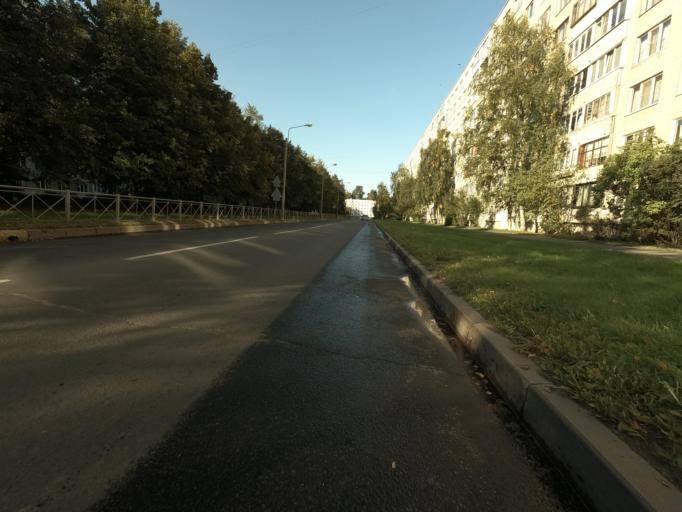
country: RU
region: St.-Petersburg
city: Kolpino
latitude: 59.7397
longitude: 30.5691
